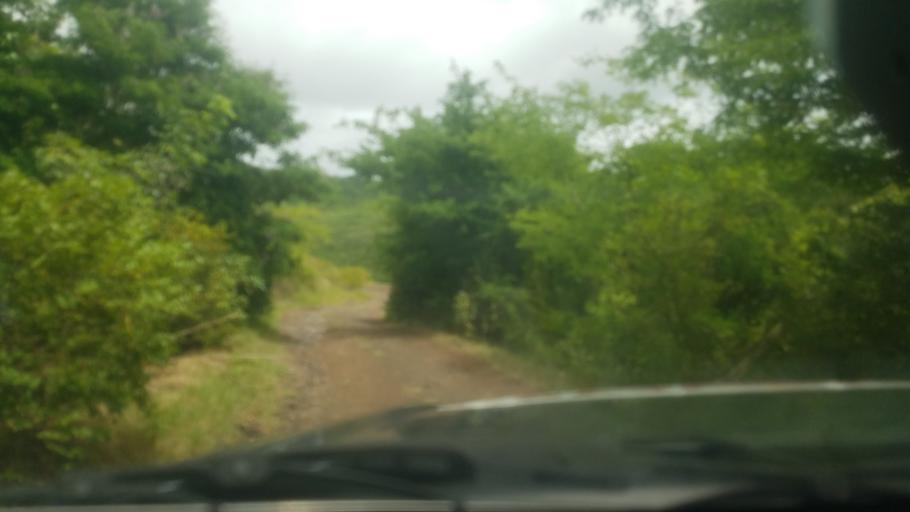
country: LC
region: Gros-Islet
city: Gros Islet
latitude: 14.0413
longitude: -60.9059
